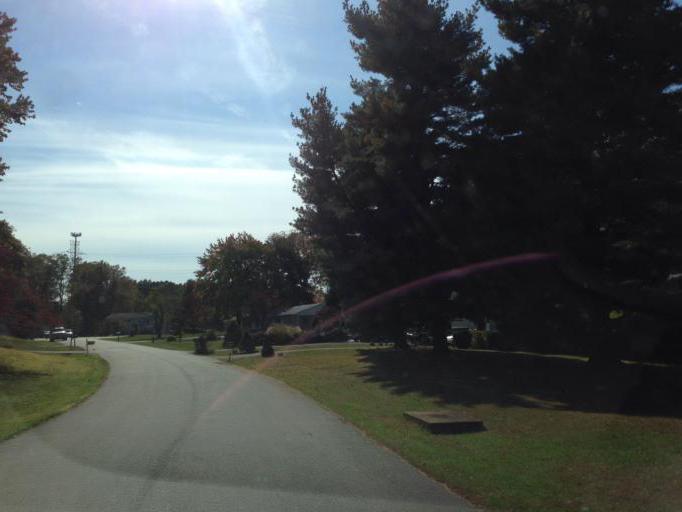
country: US
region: Maryland
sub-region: Howard County
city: Ellicott City
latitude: 39.2546
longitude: -76.8094
